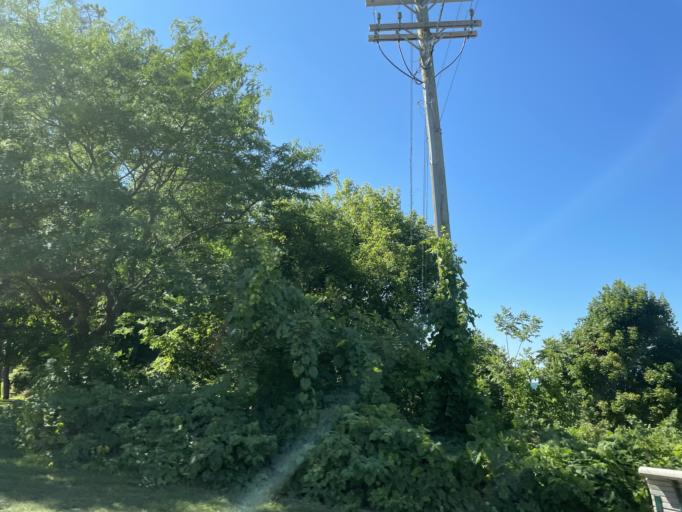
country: US
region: Michigan
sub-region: Charlevoix County
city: Charlevoix
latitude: 45.3182
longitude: -85.2642
